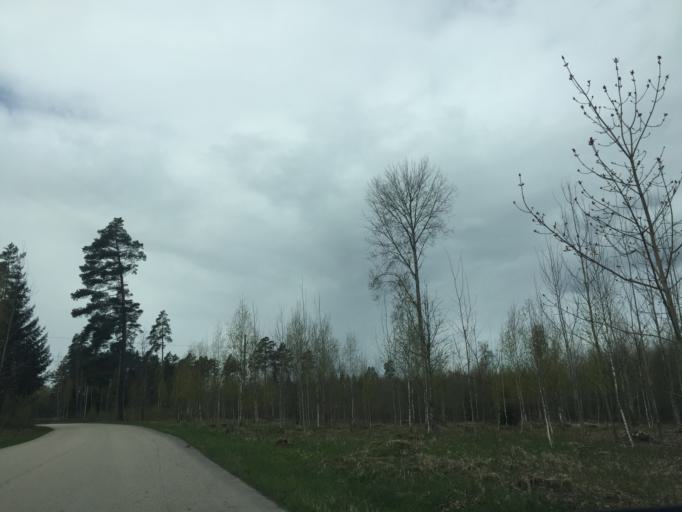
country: LV
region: Baldone
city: Baldone
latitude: 56.7633
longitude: 24.3014
